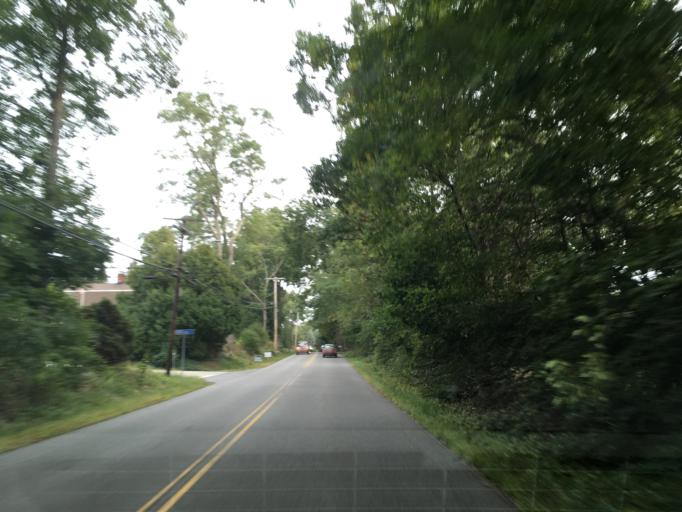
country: US
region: New Hampshire
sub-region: Rockingham County
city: Exeter
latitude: 42.9911
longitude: -70.9193
